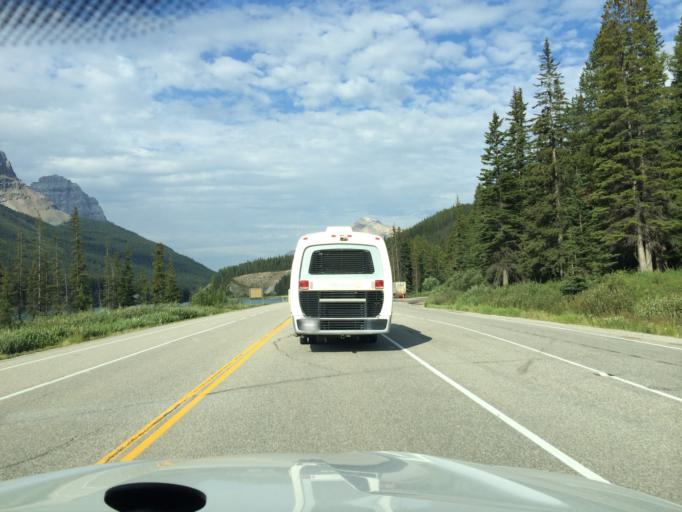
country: CA
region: Alberta
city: Lake Louise
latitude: 51.4422
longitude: -116.3436
